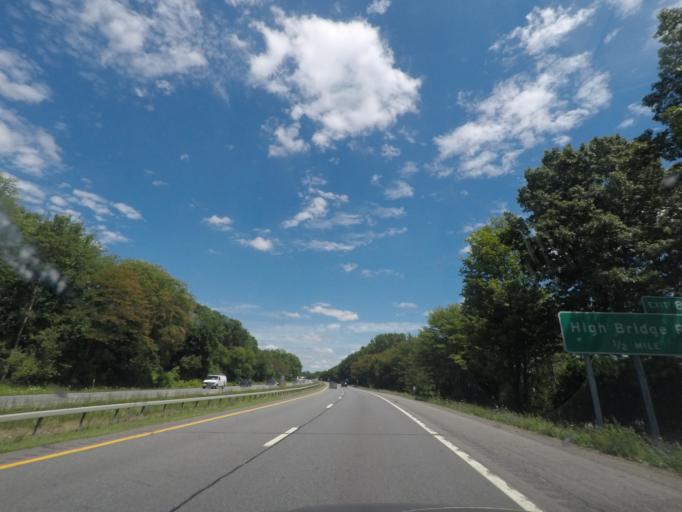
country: US
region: New York
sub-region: Schenectady County
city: Rotterdam
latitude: 42.7623
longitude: -73.9297
